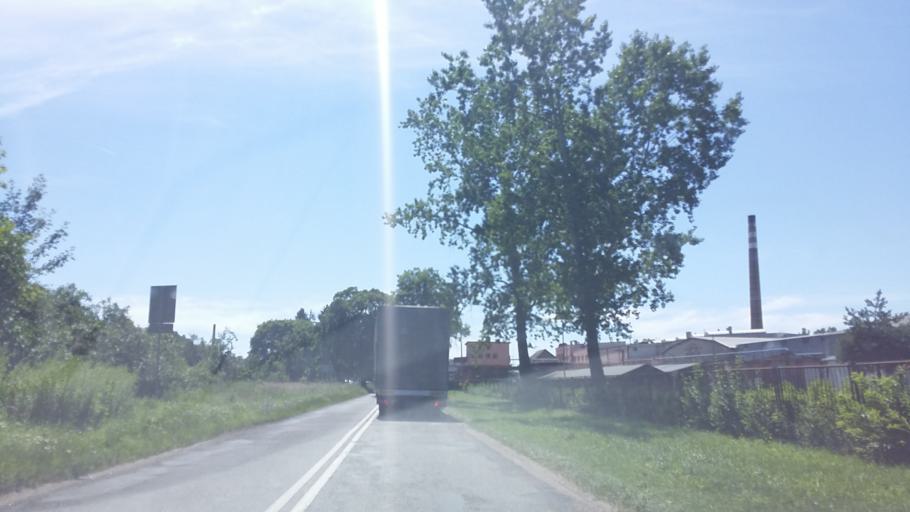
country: PL
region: West Pomeranian Voivodeship
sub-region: Powiat lobeski
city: Lobez
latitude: 53.6446
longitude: 15.6360
